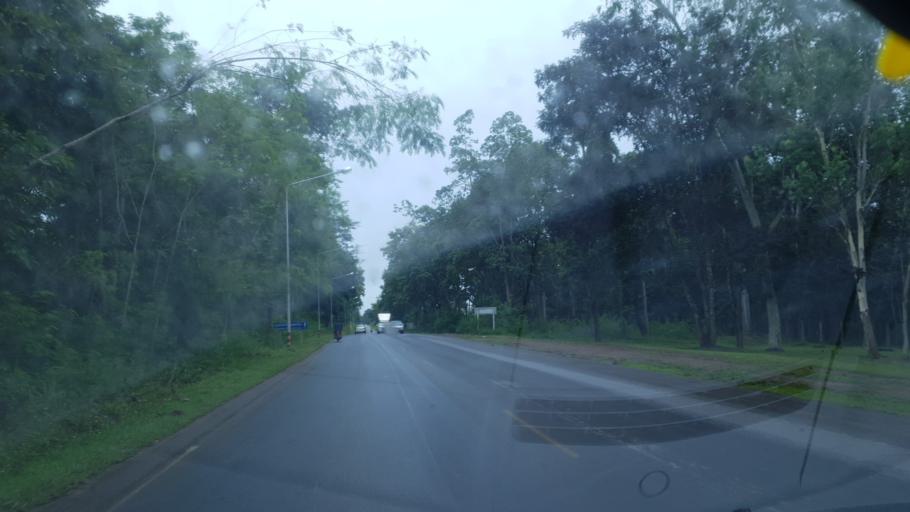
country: TH
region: Mae Hong Son
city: Pa Pae
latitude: 18.1798
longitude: 97.9346
